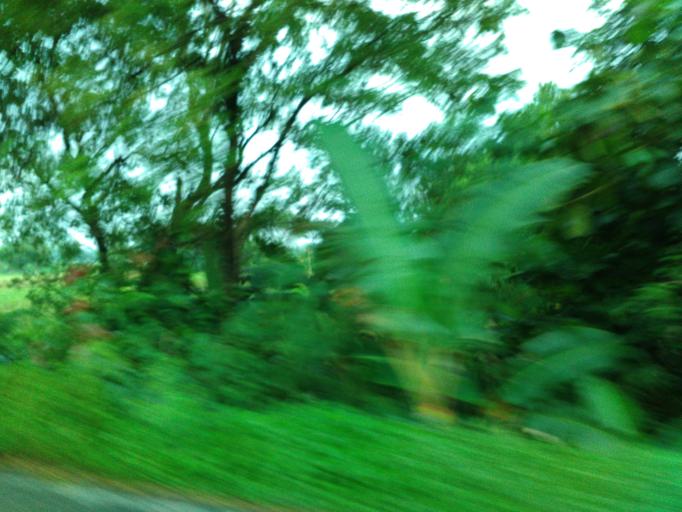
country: ID
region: Central Java
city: Ceper
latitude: -7.6563
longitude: 110.6939
